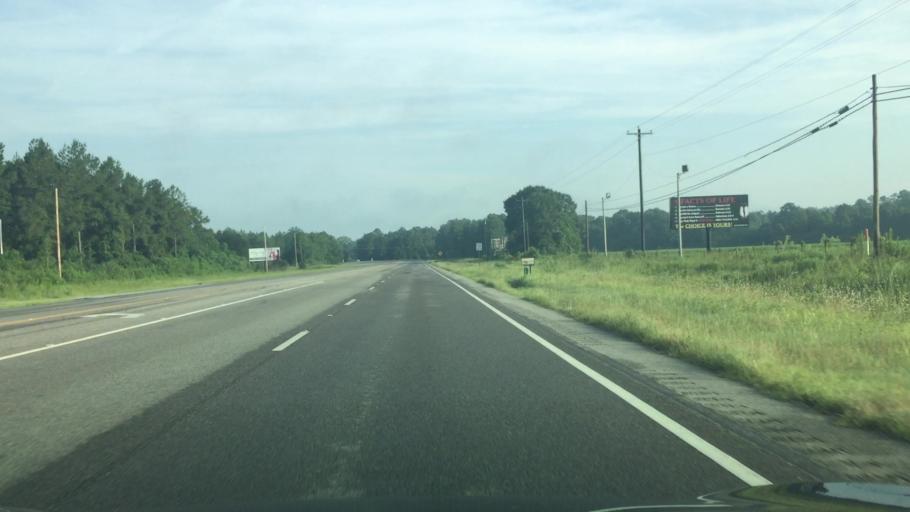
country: US
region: Alabama
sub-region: Covington County
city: Andalusia
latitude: 31.3418
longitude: -86.5234
